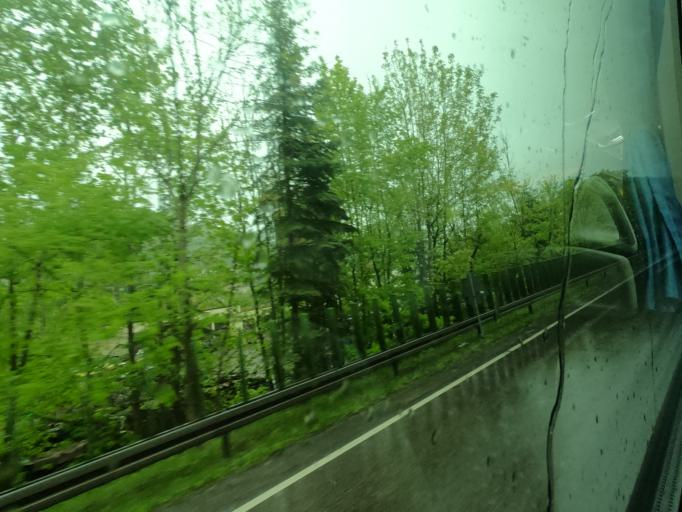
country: DE
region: Baden-Wuerttemberg
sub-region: Regierungsbezirk Stuttgart
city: Aalen
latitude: 48.8165
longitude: 10.1218
